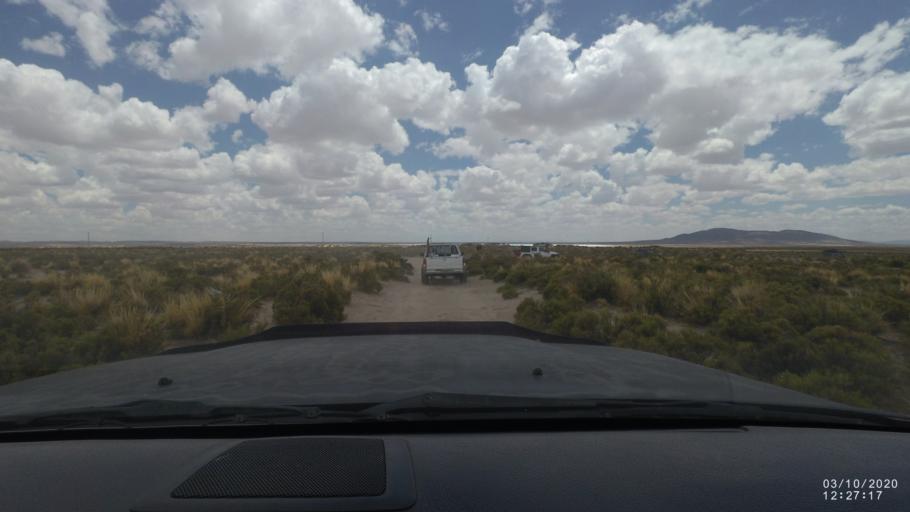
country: BO
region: Oruro
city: Poopo
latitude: -18.6937
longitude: -67.5545
